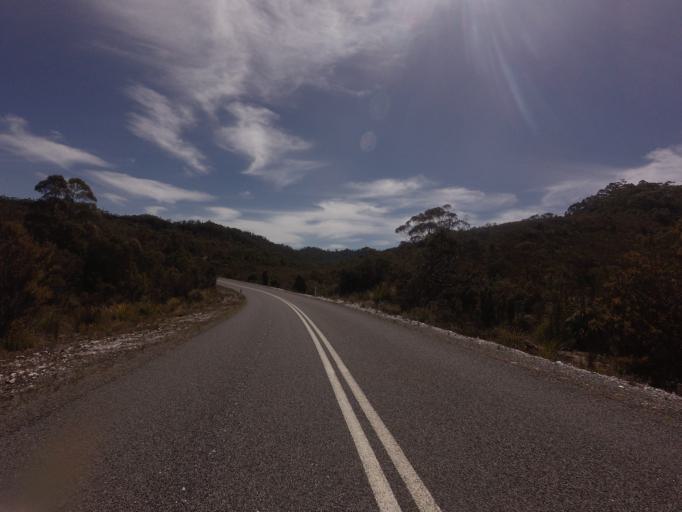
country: AU
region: Tasmania
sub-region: Huon Valley
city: Geeveston
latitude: -42.8206
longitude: 146.1232
